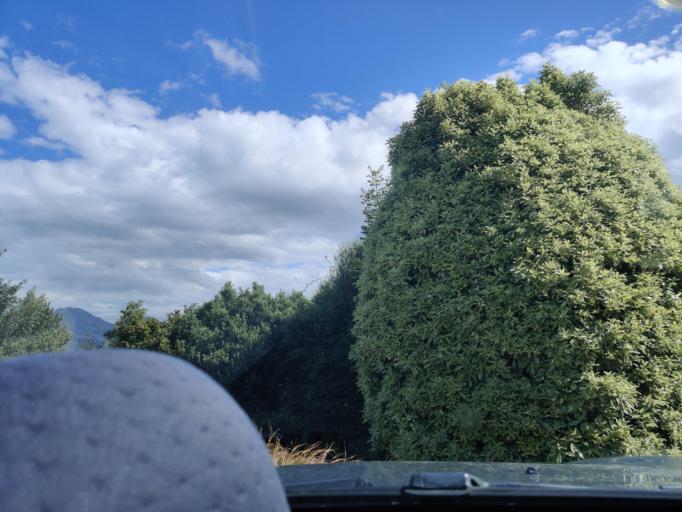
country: NZ
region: Canterbury
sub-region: Hurunui District
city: Amberley
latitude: -42.5259
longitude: 172.8295
